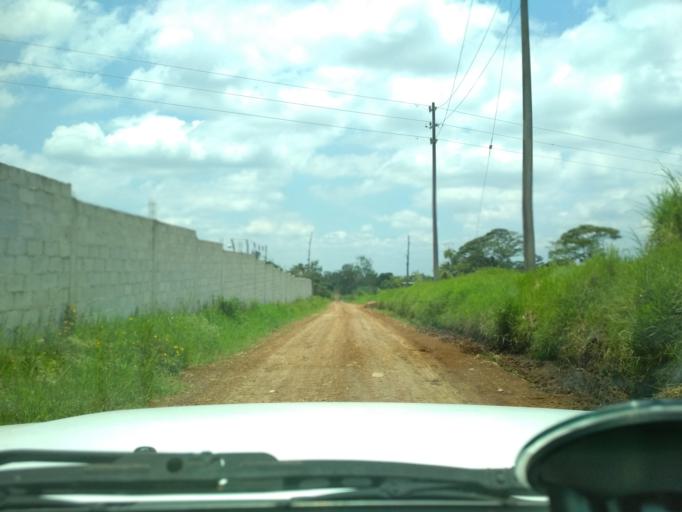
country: MX
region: Veracruz
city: Tocuila
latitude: 18.9477
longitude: -97.0155
